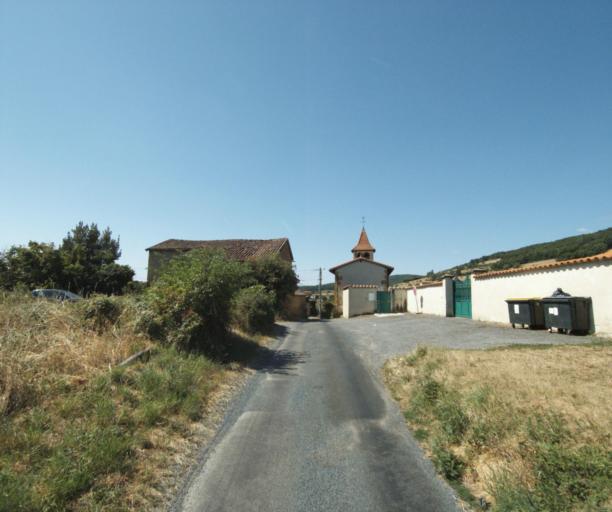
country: FR
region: Rhone-Alpes
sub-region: Departement du Rhone
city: Bessenay
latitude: 45.8000
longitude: 4.5491
